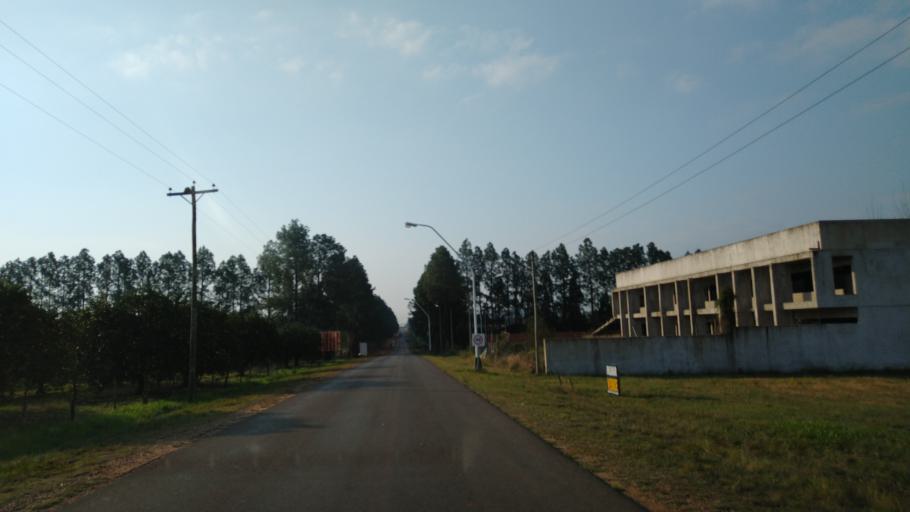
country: AR
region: Entre Rios
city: Santa Ana
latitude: -30.9102
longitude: -57.9263
